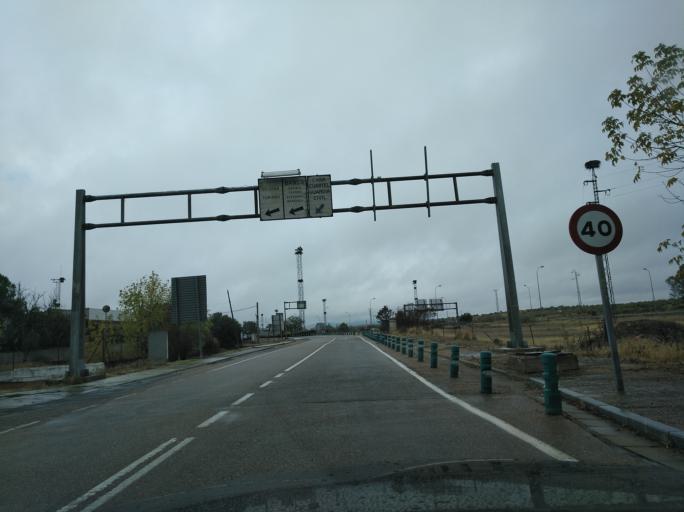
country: ES
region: Extremadura
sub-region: Provincia de Badajoz
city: Badajoz
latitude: 38.8836
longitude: -7.0287
